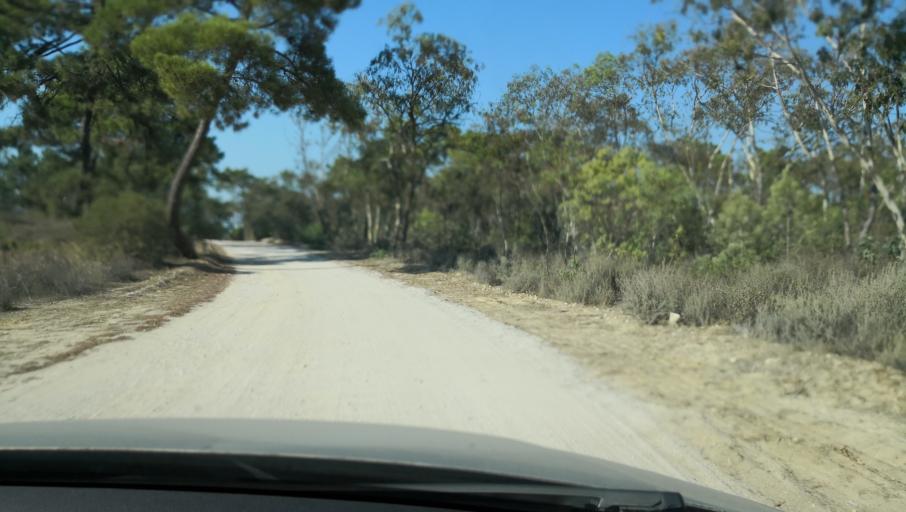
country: PT
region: Setubal
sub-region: Setubal
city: Setubal
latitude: 38.4719
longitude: -8.8782
